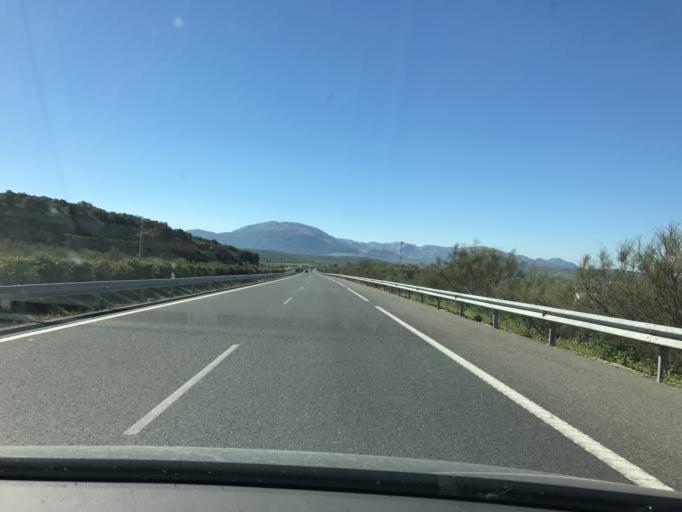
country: ES
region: Andalusia
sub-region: Provincia de Malaga
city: Villanueva del Trabuco
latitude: 37.0961
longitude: -4.3158
